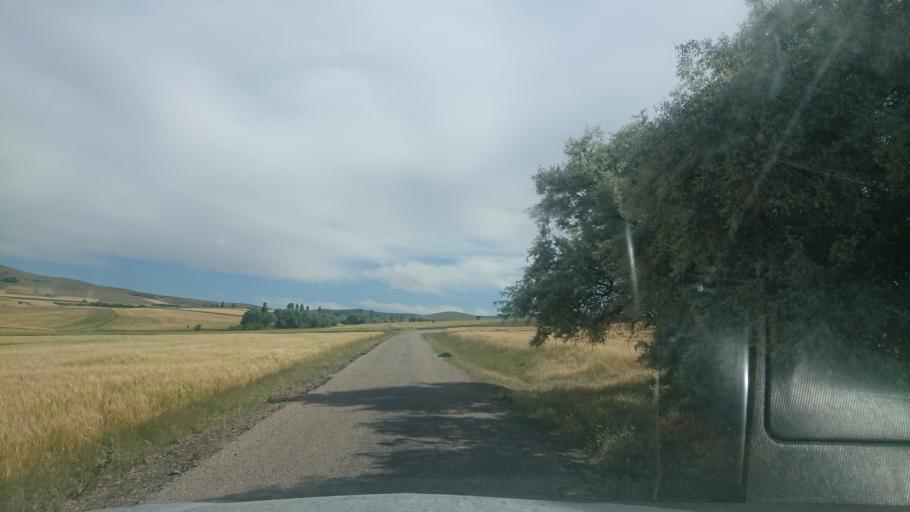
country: TR
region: Aksaray
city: Ortakoy
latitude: 38.8184
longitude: 34.0029
